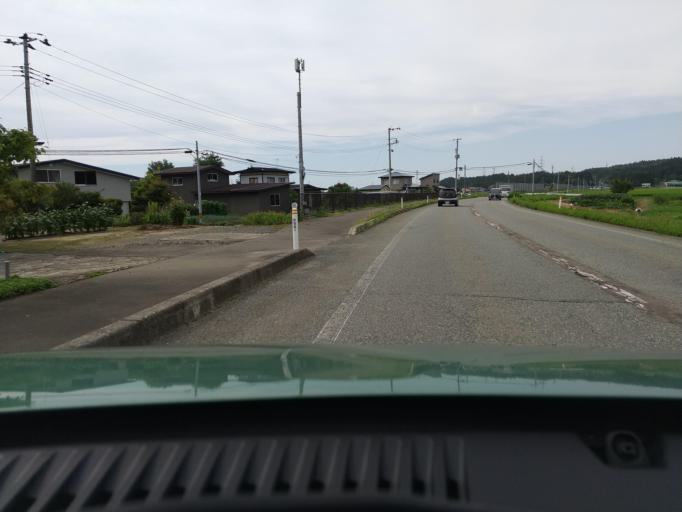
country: JP
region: Akita
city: Akita Shi
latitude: 39.7966
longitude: 140.0957
